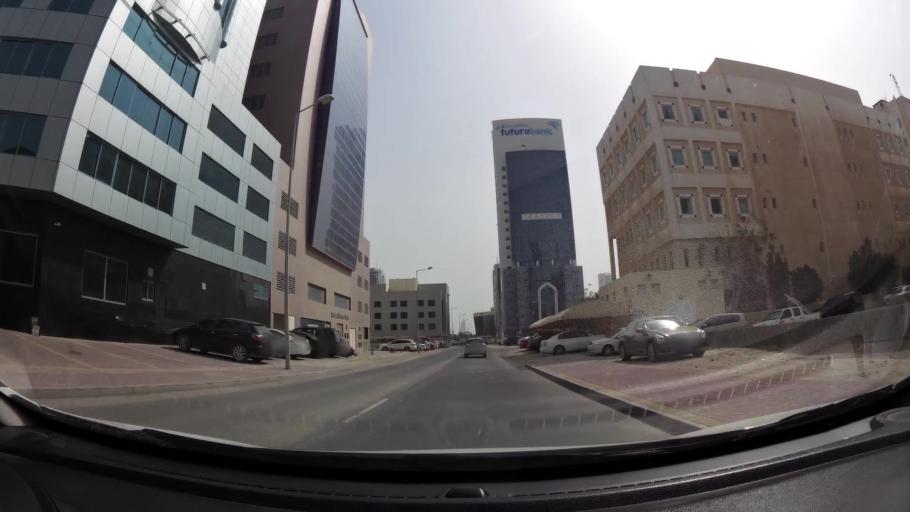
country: BH
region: Manama
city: Jidd Hafs
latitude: 26.2378
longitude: 50.5384
